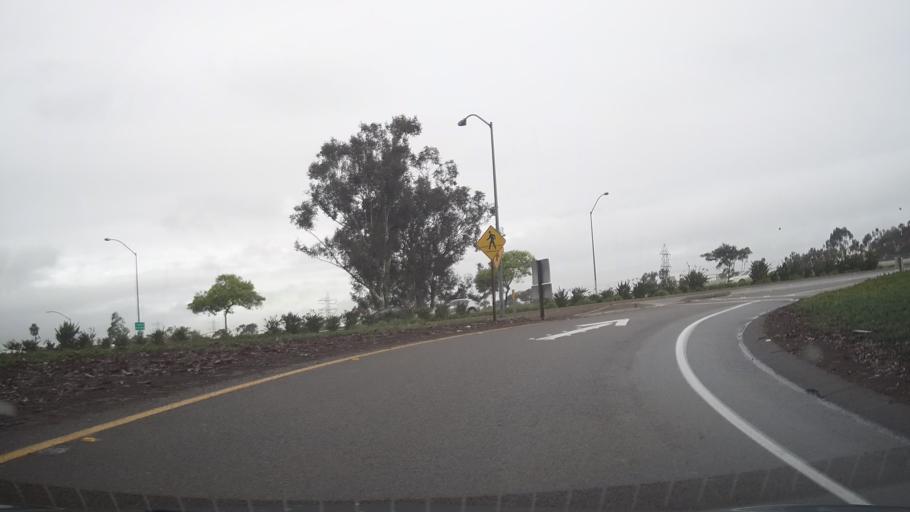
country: US
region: California
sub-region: San Diego County
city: San Diego
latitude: 32.8211
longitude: -117.1636
